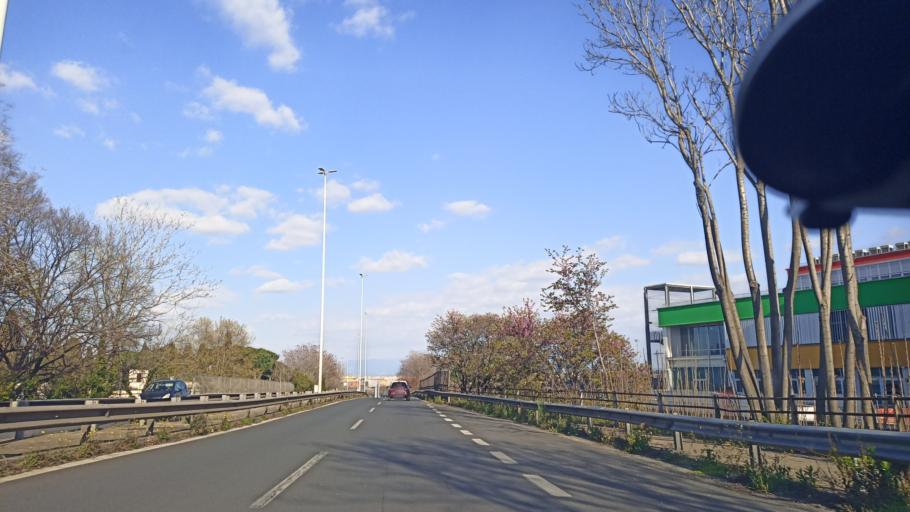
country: IT
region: Latium
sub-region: Citta metropolitana di Roma Capitale
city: Rome
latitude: 41.8971
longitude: 12.5207
